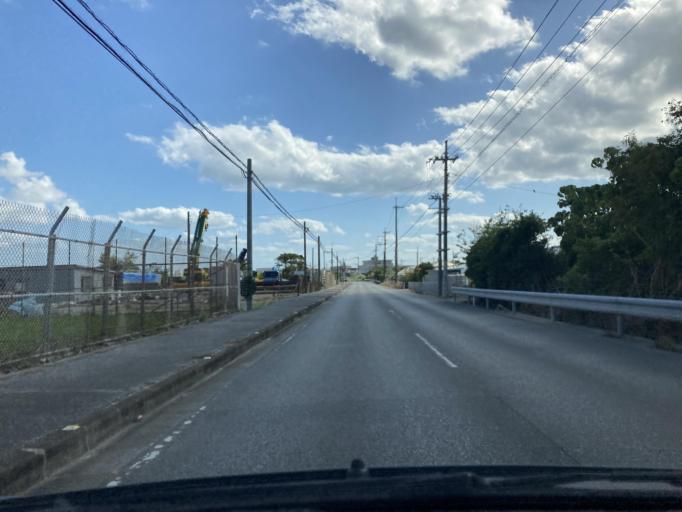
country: JP
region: Okinawa
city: Gushikawa
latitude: 26.3466
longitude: 127.8471
